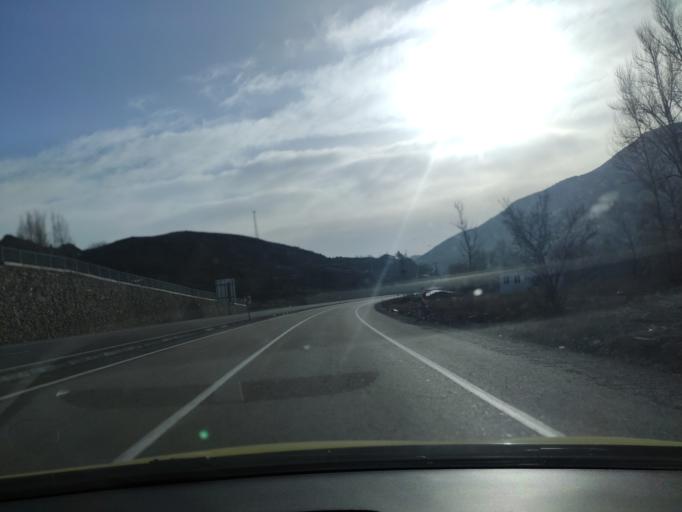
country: TR
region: Gumushane
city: Kale
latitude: 40.4048
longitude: 39.6181
